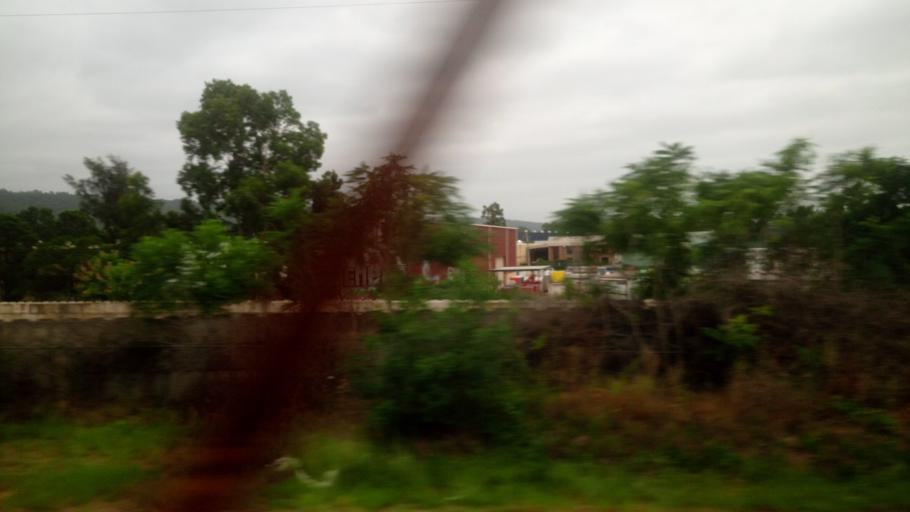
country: AU
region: New South Wales
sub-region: Penrith Municipality
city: Emu Heights
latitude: -33.7483
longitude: 150.6580
